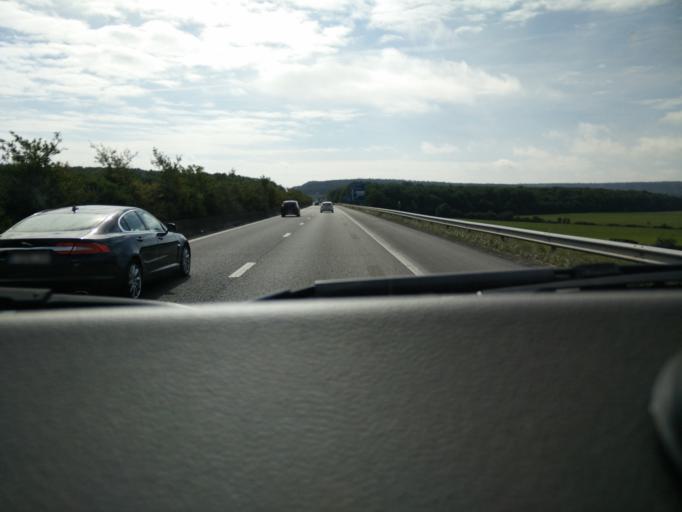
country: BE
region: Wallonia
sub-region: Province du Luxembourg
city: Wellin
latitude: 50.1271
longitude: 5.0918
